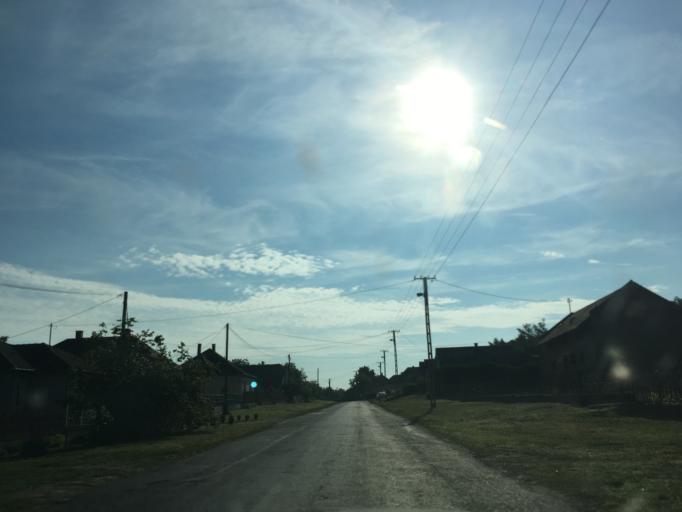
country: HU
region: Szabolcs-Szatmar-Bereg
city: Nyirlugos
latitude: 47.6958
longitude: 22.0527
